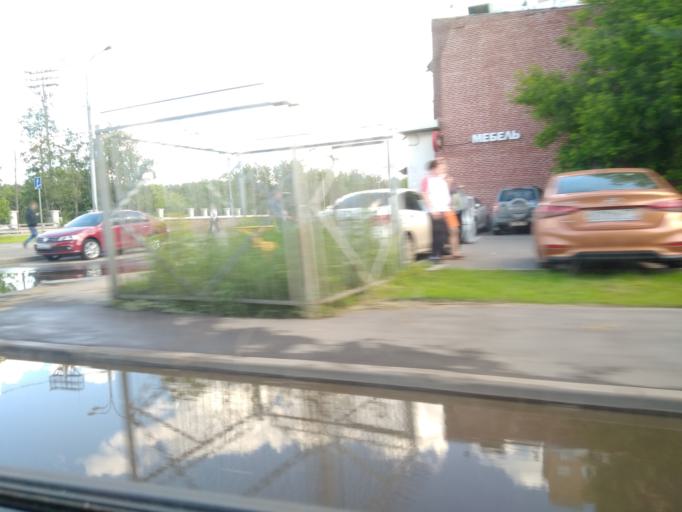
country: RU
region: Moskovskaya
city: Koptevo
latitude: 55.8341
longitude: 37.5333
